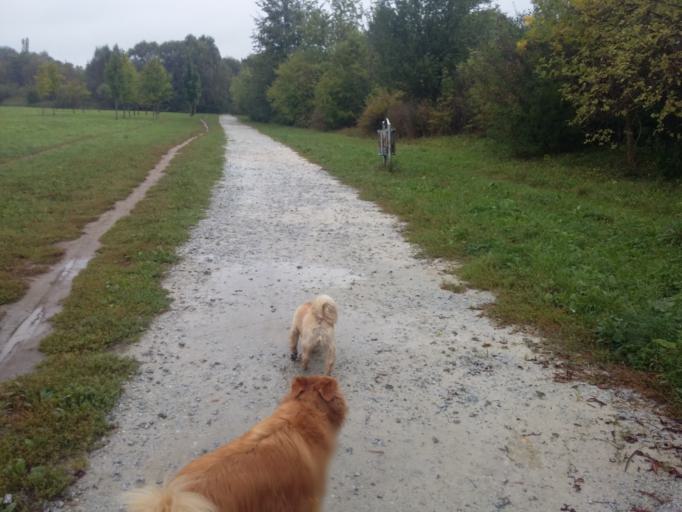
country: PL
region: Lodz Voivodeship
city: Lodz
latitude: 51.7525
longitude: 19.3971
